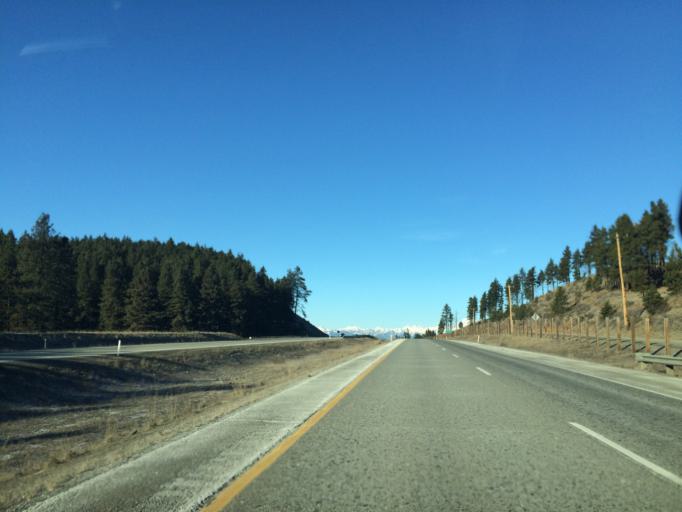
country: US
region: Washington
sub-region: Kittitas County
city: Cle Elum
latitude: 47.1239
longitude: -120.8015
